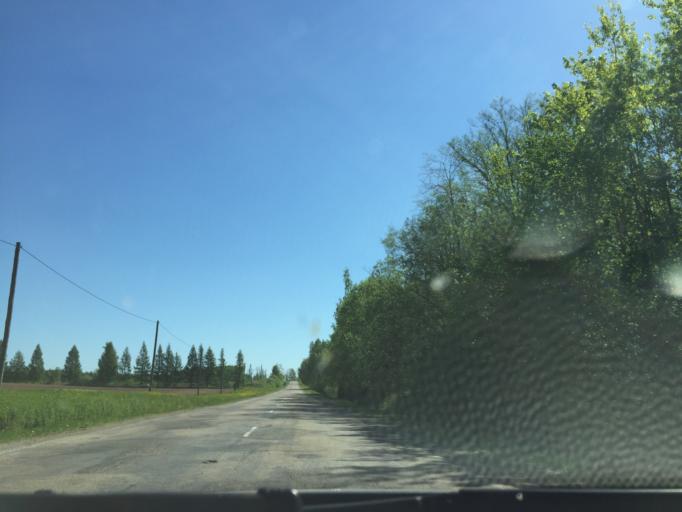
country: LV
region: Malpils
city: Malpils
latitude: 57.0199
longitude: 24.9166
